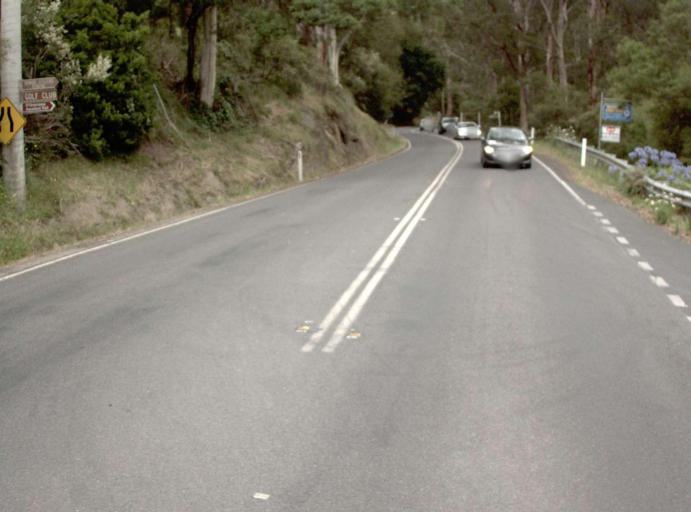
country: AU
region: Victoria
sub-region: Yarra Ranges
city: Millgrove
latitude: -37.7555
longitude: 145.6793
